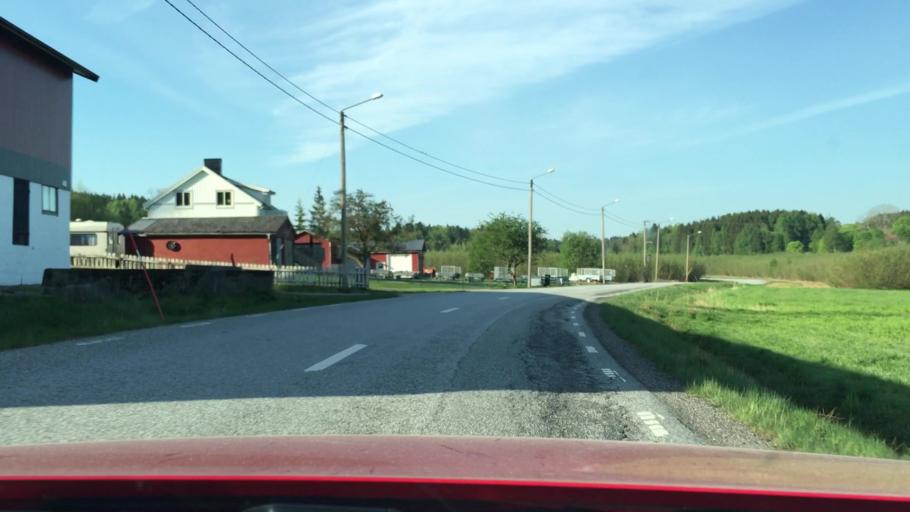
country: SE
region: Vaestra Goetaland
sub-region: Munkedals Kommun
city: Munkedal
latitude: 58.6006
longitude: 11.5558
